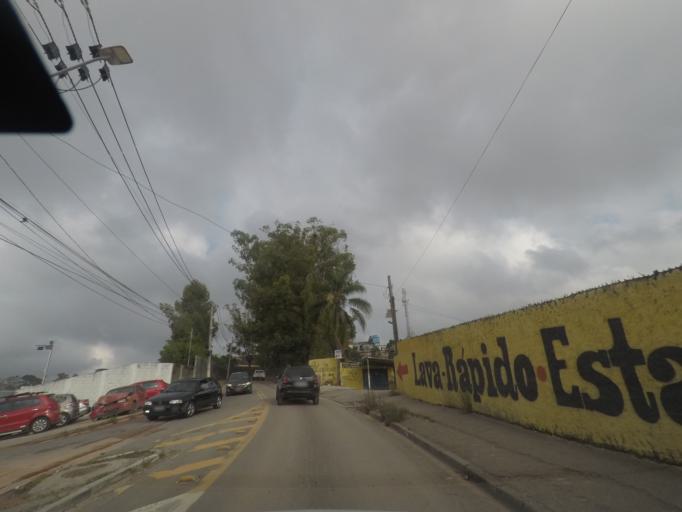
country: BR
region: Sao Paulo
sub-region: Osasco
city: Osasco
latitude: -23.5783
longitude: -46.7788
